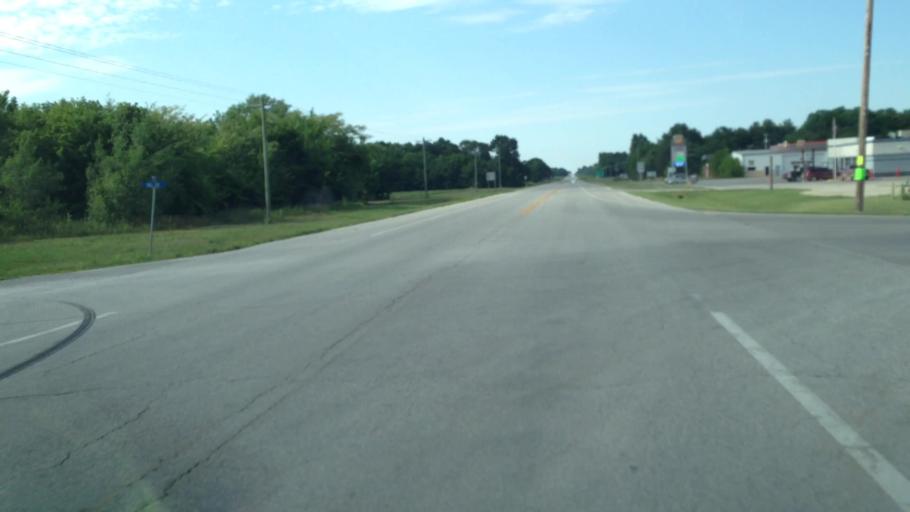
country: US
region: Kansas
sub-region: Neosho County
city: Erie
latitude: 37.5722
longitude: -95.2525
